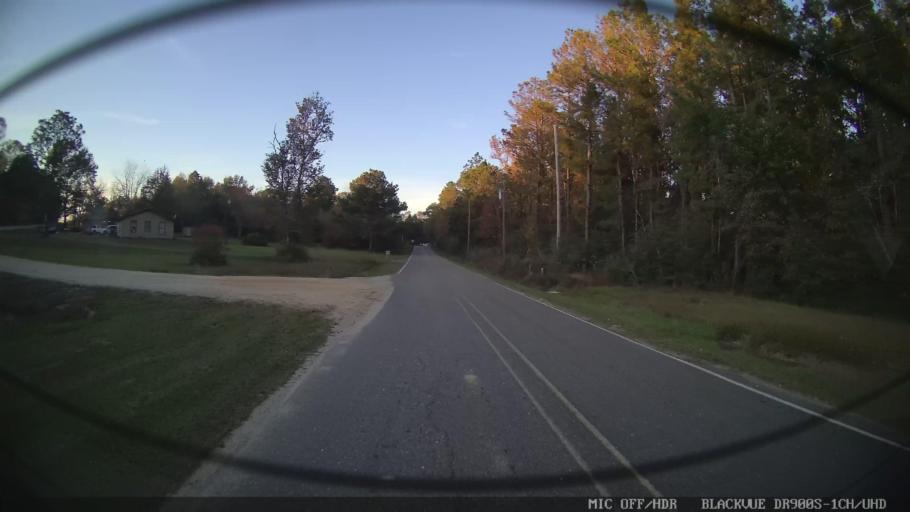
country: US
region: Mississippi
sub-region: Stone County
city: Wiggins
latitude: 30.9872
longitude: -89.2589
